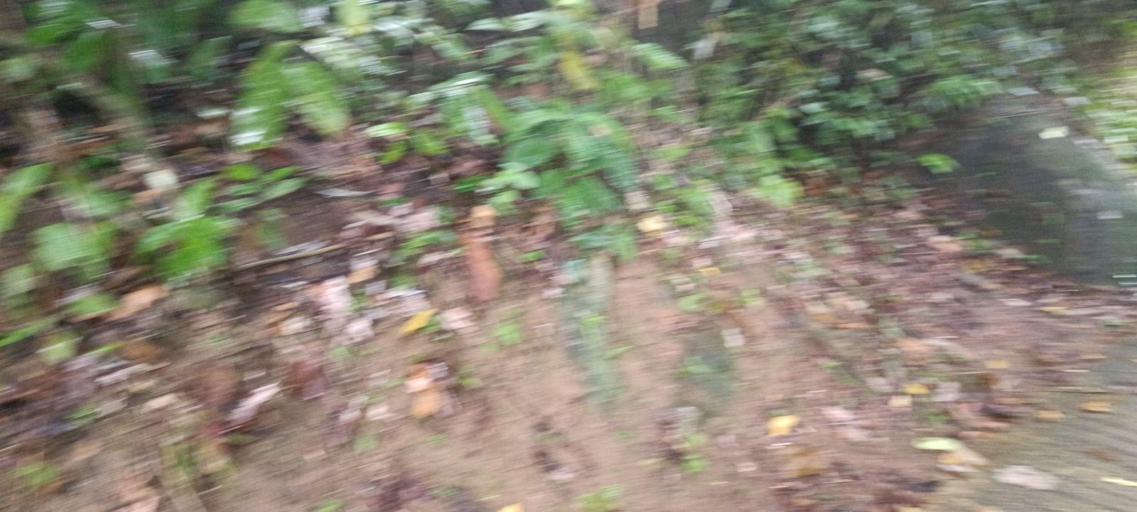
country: MY
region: Penang
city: Bukit Mertajam
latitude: 5.3657
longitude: 100.4749
